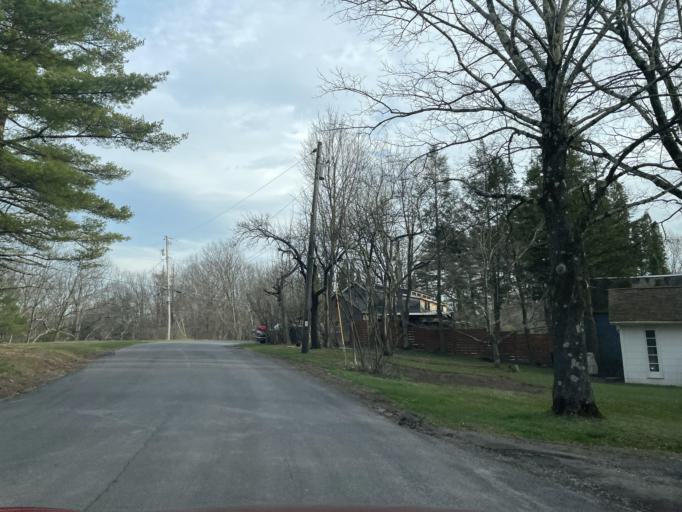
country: US
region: New York
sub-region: Ulster County
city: Manorville
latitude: 42.1421
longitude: -74.0361
